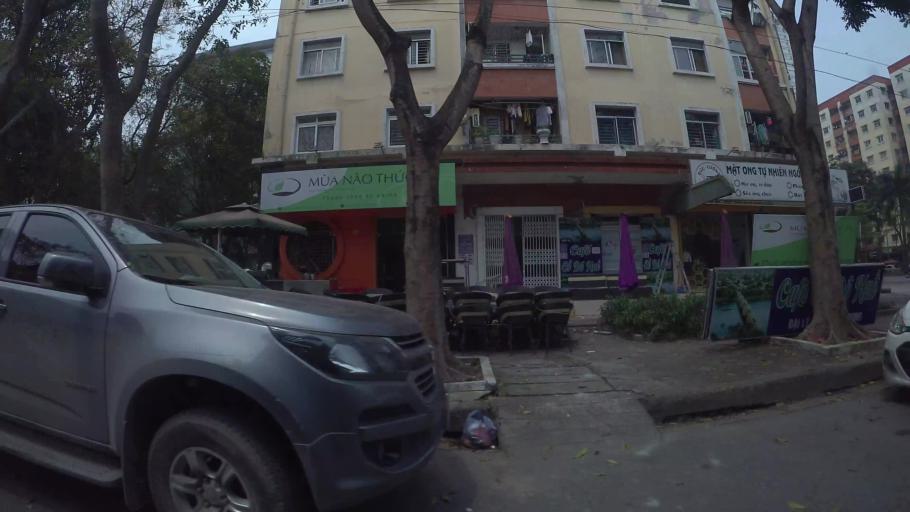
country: VN
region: Ha Noi
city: Van Dien
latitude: 20.9637
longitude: 105.8327
